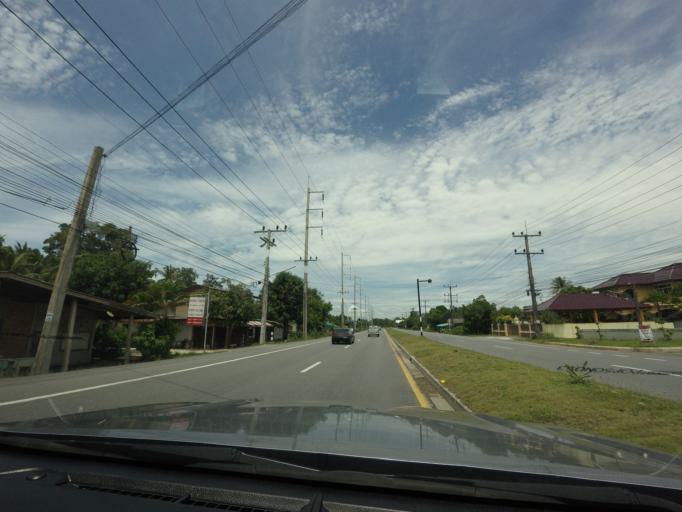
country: TH
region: Songkhla
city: Krasae Sin
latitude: 7.5918
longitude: 100.4043
